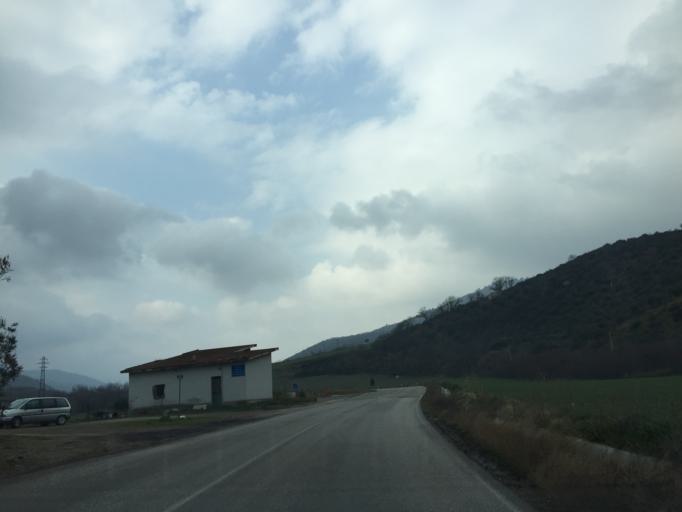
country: IT
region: Apulia
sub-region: Provincia di Foggia
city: Bovino
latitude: 41.2753
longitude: 15.3628
